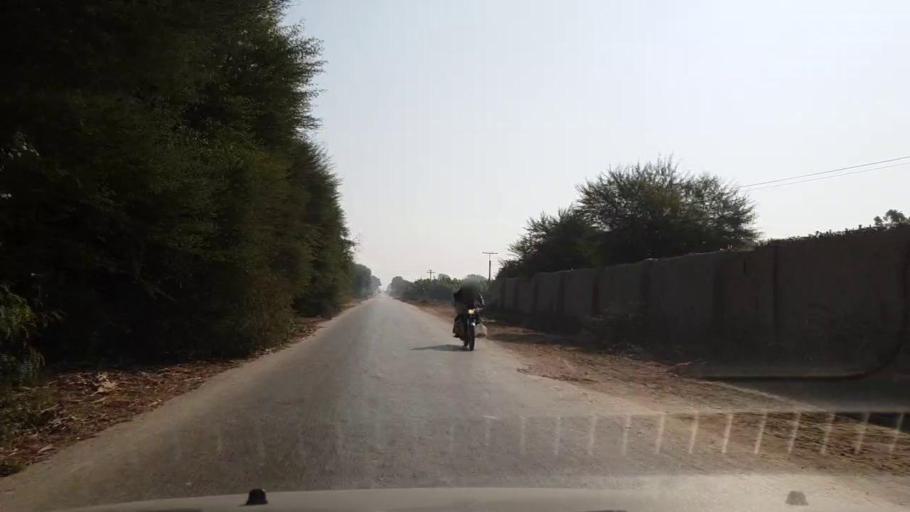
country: PK
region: Sindh
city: Tando Jam
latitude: 25.5277
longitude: 68.5823
